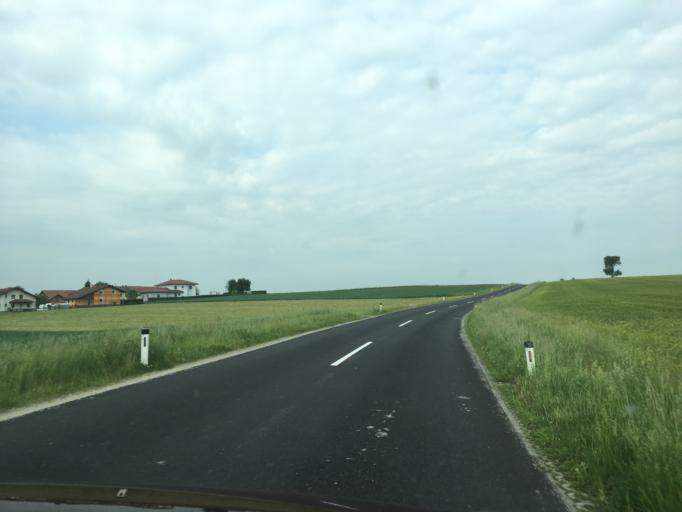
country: AT
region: Upper Austria
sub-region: Politischer Bezirk Grieskirchen
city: Grieskirchen
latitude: 48.2839
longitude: 13.7974
